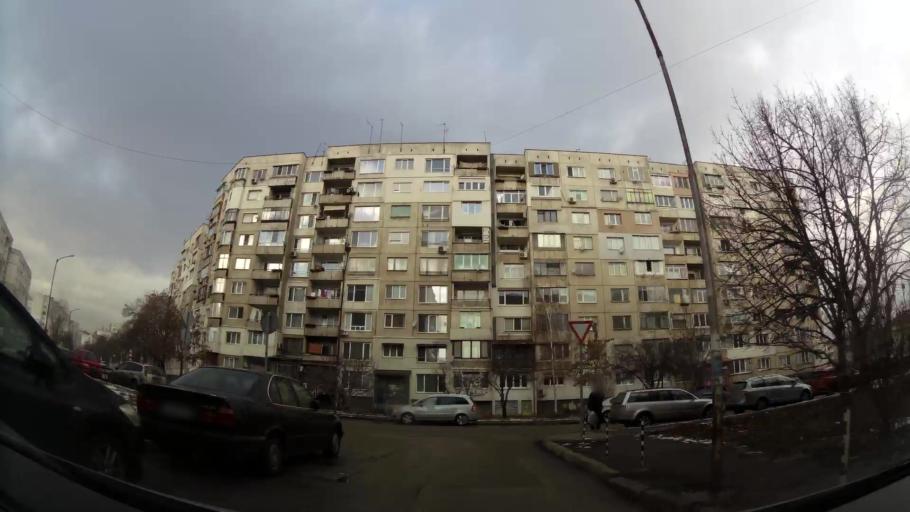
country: BG
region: Sofia-Capital
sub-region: Stolichna Obshtina
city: Sofia
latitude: 42.7003
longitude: 23.2922
